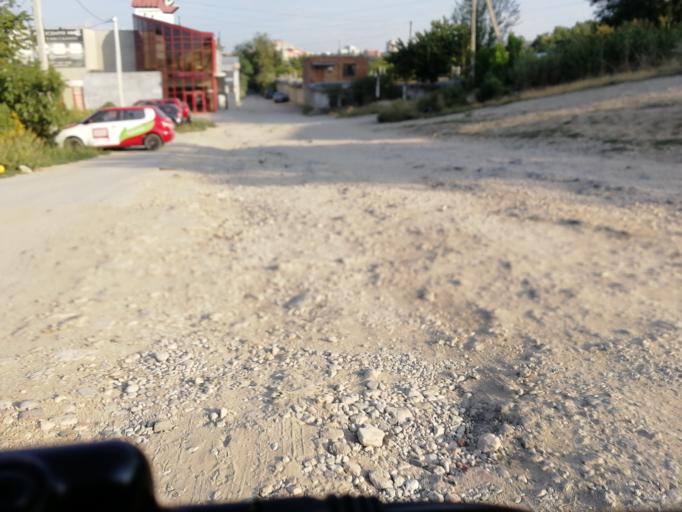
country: MD
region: Chisinau
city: Chisinau
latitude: 47.0276
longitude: 28.8708
